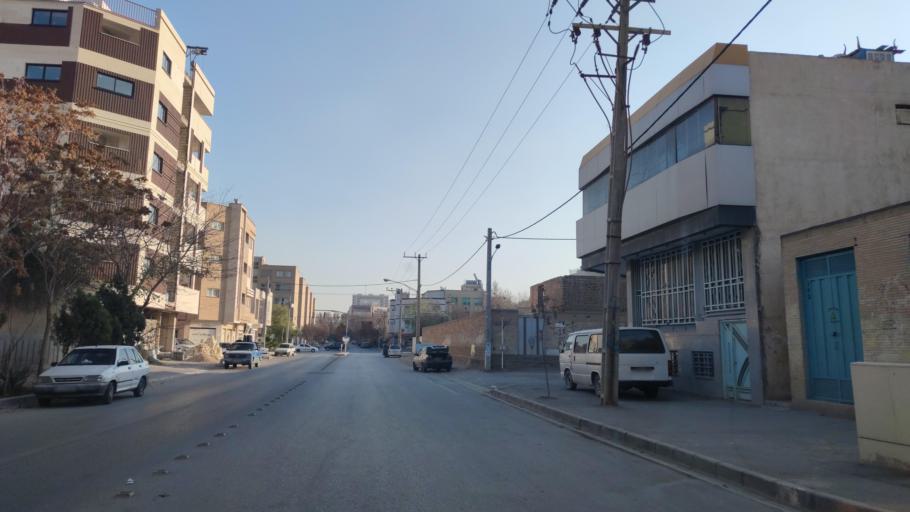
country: IR
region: Isfahan
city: Isfahan
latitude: 32.7105
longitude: 51.6855
